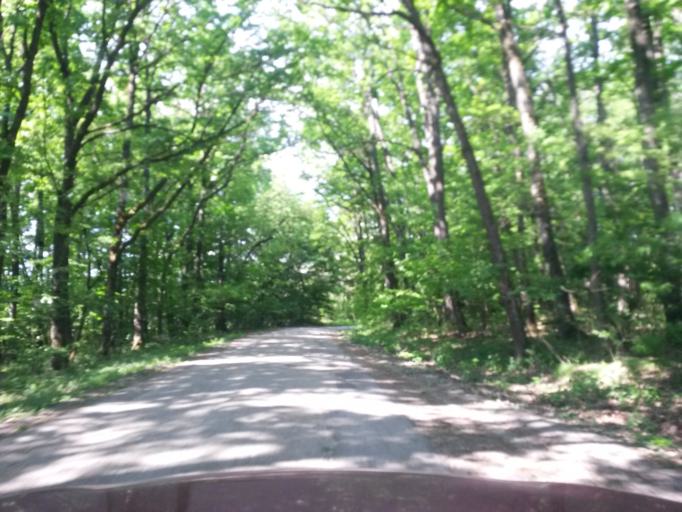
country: SK
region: Kosicky
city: Moldava nad Bodvou
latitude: 48.7107
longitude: 21.0208
